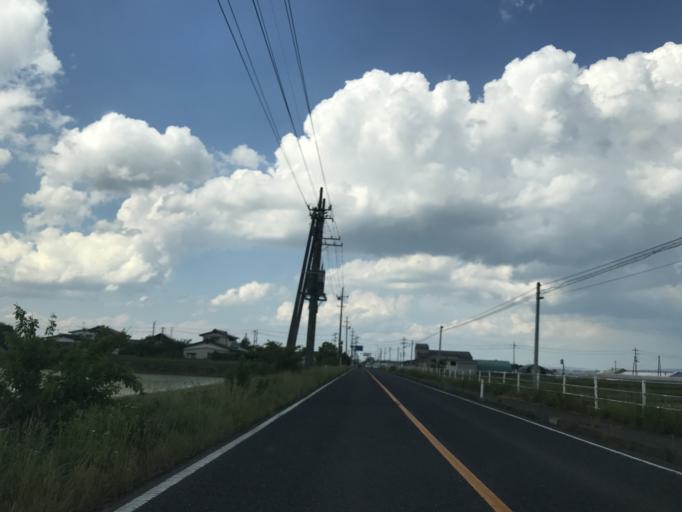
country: JP
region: Miyagi
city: Wakuya
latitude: 38.6046
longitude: 141.1721
